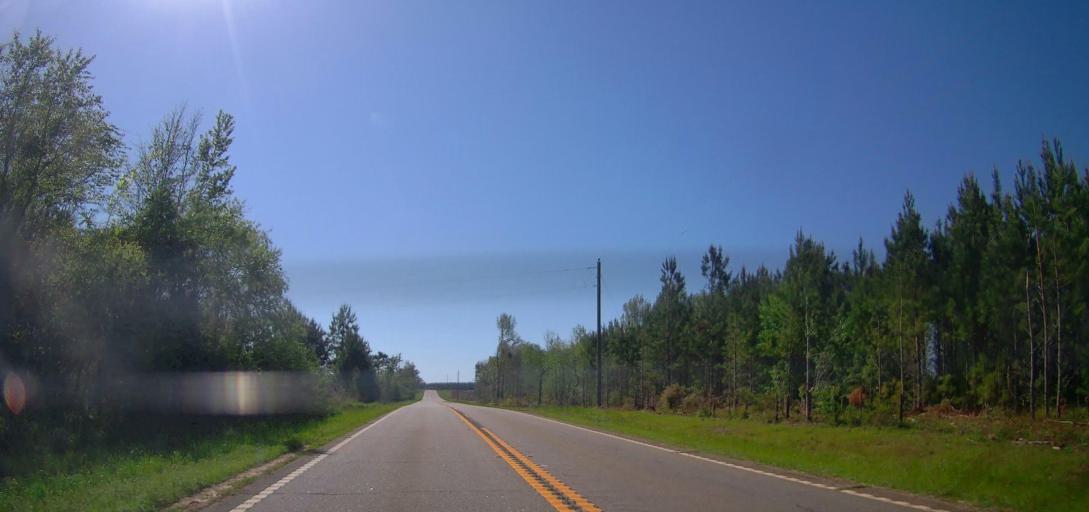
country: US
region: Georgia
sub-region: Dooly County
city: Unadilla
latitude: 32.2534
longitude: -83.6254
